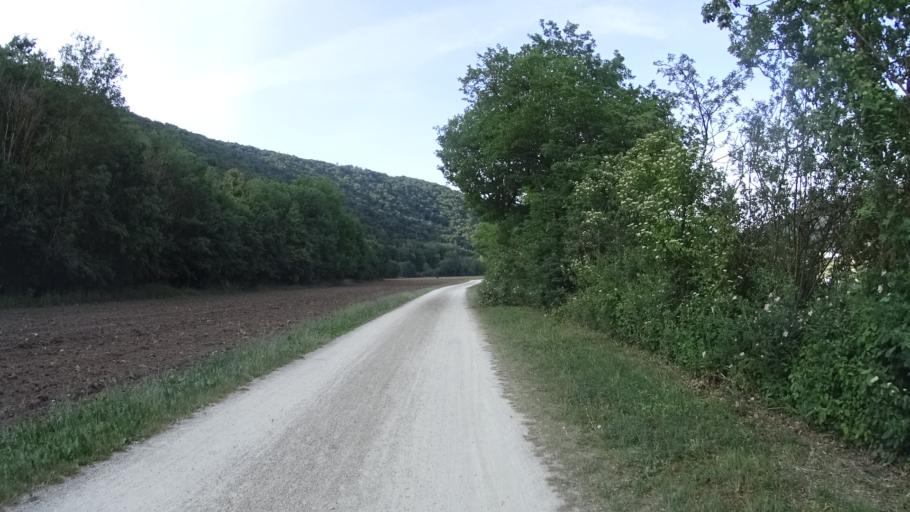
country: DE
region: Bavaria
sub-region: Lower Bavaria
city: Riedenburg
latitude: 48.9813
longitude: 11.6953
